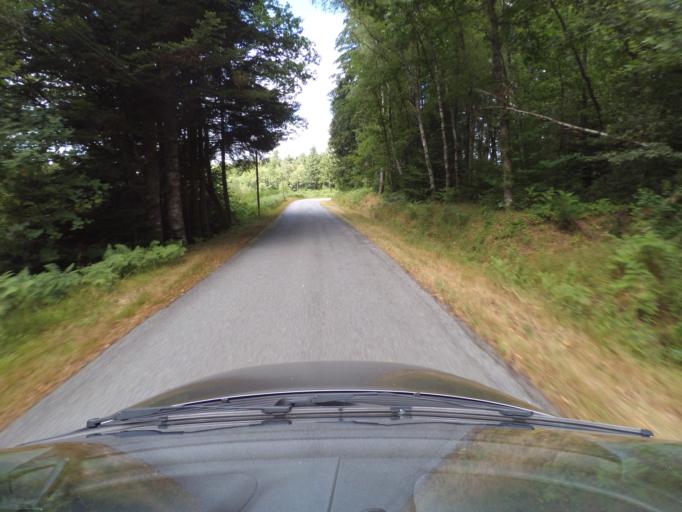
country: FR
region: Limousin
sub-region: Departement de la Creuse
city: Banize
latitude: 45.7657
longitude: 1.9475
